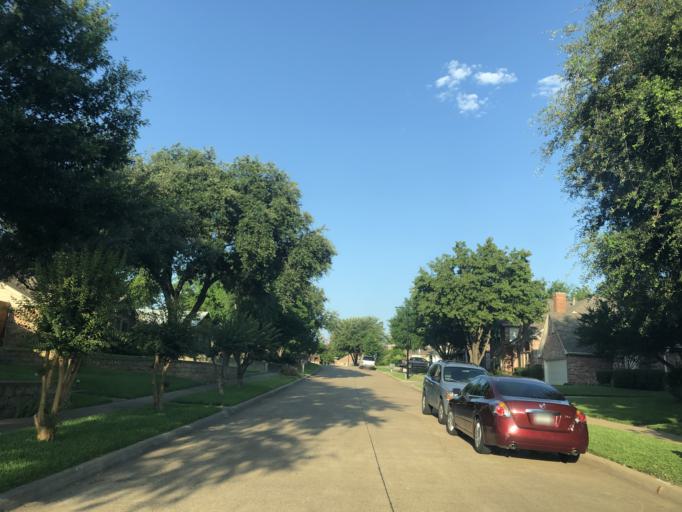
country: US
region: Texas
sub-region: Dallas County
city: Sunnyvale
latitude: 32.8449
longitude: -96.6087
